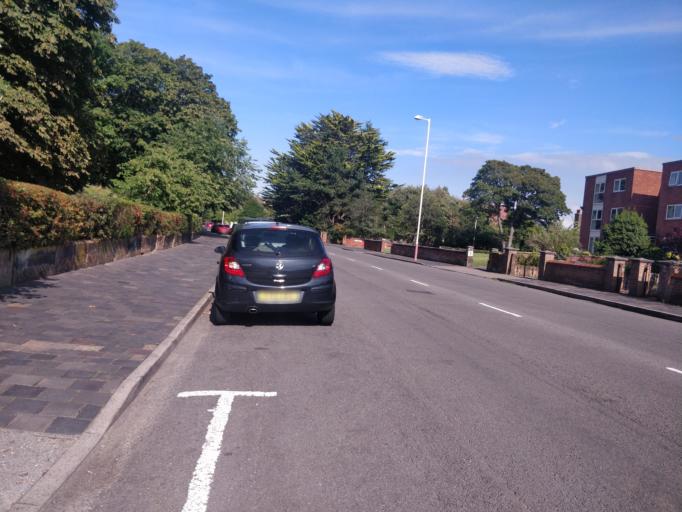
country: GB
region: England
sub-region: Sefton
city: Southport
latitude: 53.6551
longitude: -2.9861
